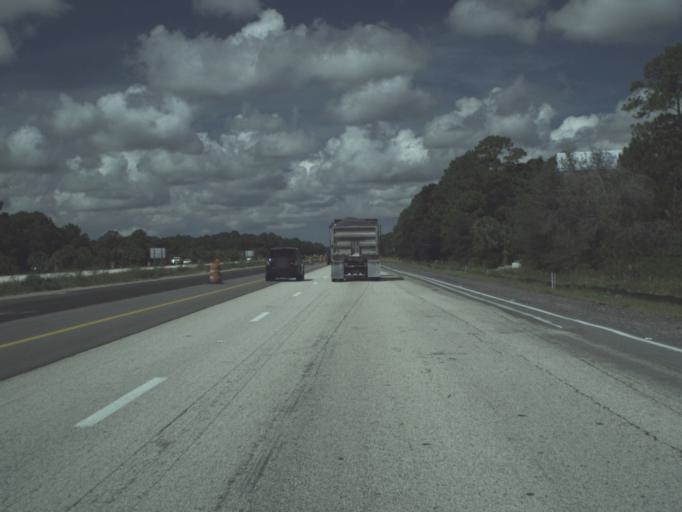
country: US
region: Florida
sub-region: Sarasota County
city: North Port
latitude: 27.0991
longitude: -82.1613
